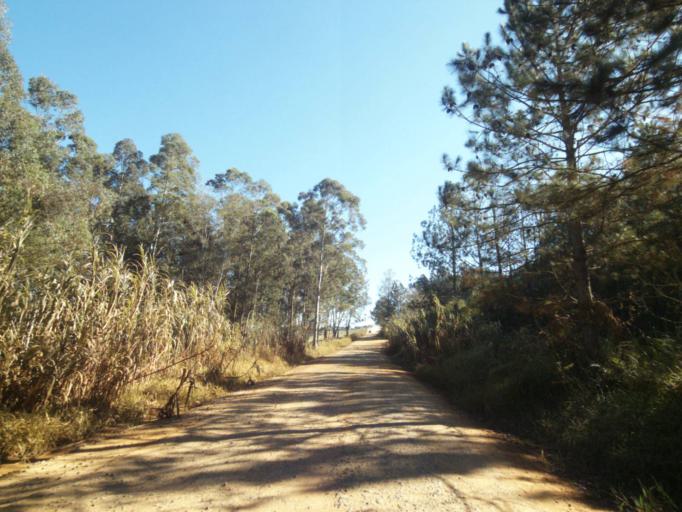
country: BR
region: Parana
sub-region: Tibagi
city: Tibagi
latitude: -24.5323
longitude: -50.3772
